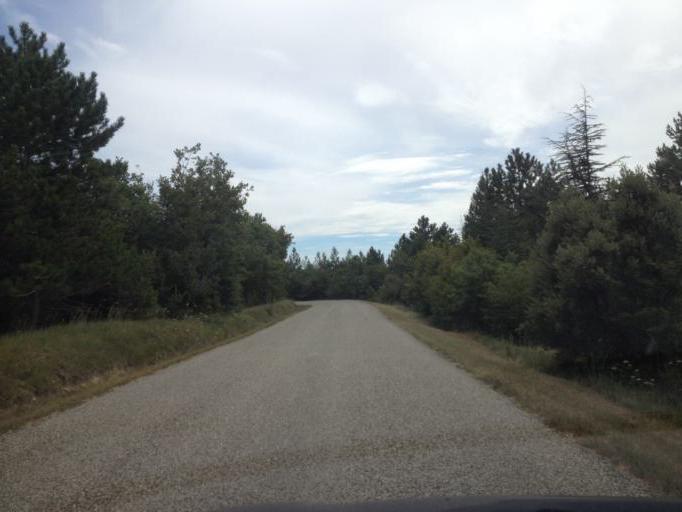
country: FR
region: Rhone-Alpes
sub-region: Departement de la Drome
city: Allan
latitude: 44.4661
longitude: 4.8236
